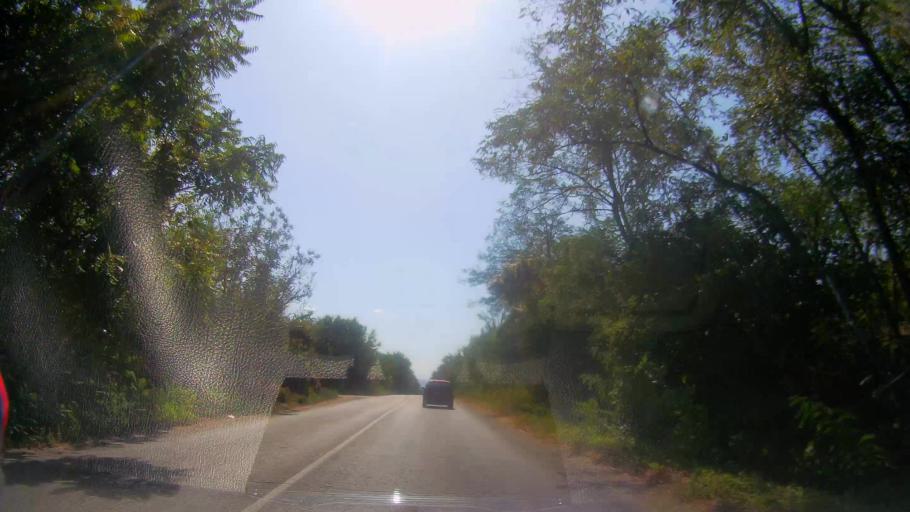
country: BG
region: Veliko Turnovo
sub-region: Obshtina Gorna Oryakhovitsa
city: Purvomaytsi
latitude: 43.2550
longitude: 25.6427
